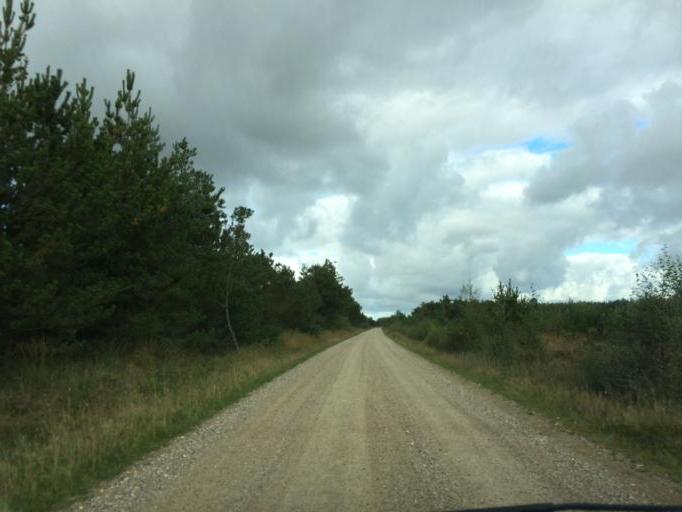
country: DK
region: Central Jutland
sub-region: Holstebro Kommune
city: Ulfborg
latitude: 56.2808
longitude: 8.3954
